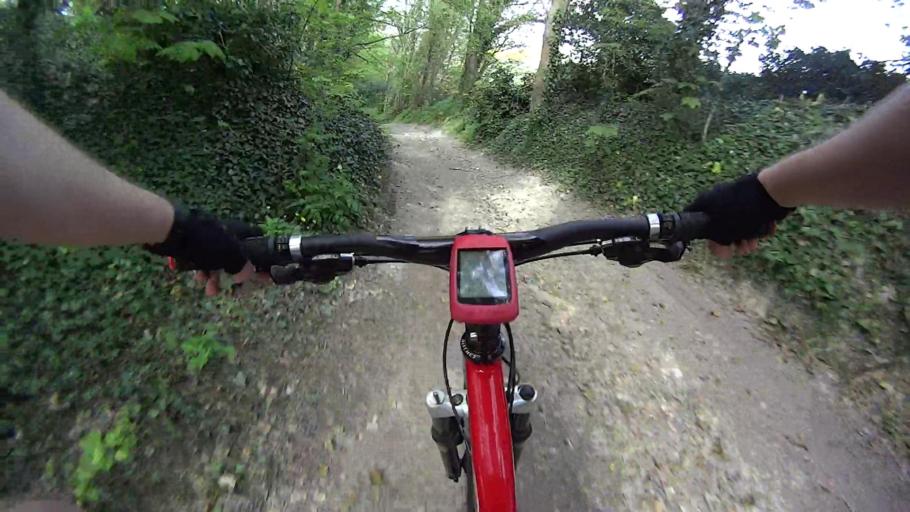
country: GB
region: England
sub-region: East Sussex
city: Seaford
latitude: 50.8096
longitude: 0.1697
